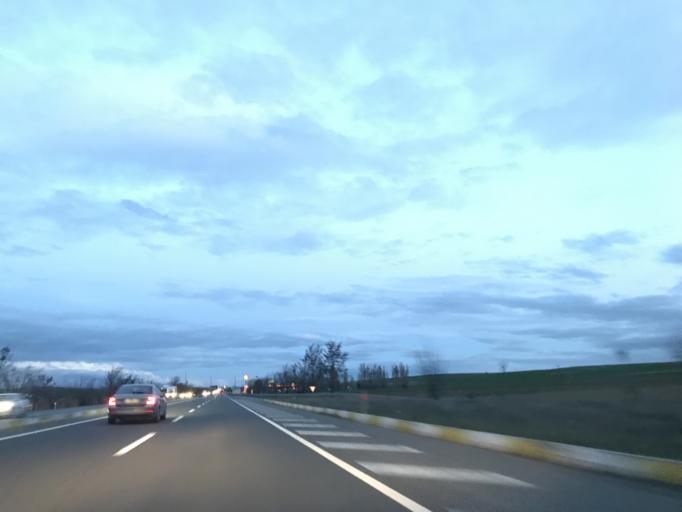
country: TR
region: Konya
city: Kulu
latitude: 39.2013
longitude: 33.0878
